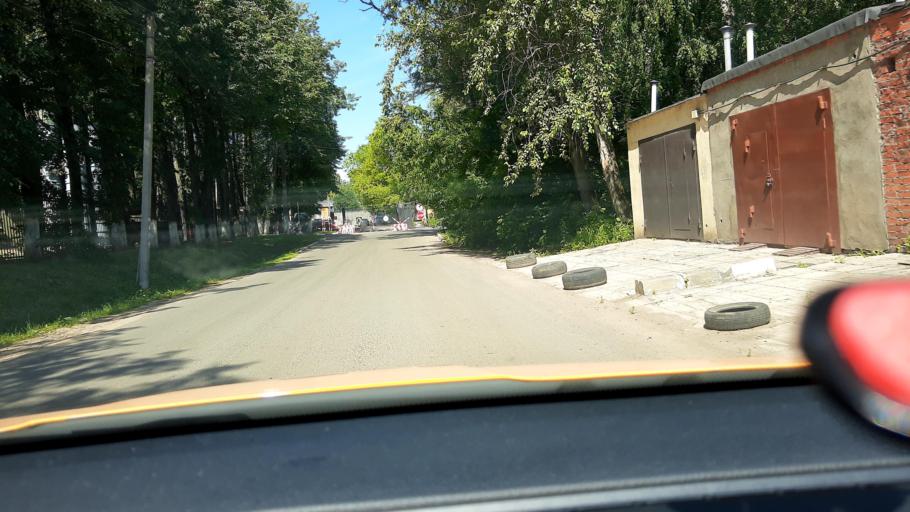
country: RU
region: Moskovskaya
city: Dolgoprudnyy
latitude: 55.9505
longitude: 37.5261
